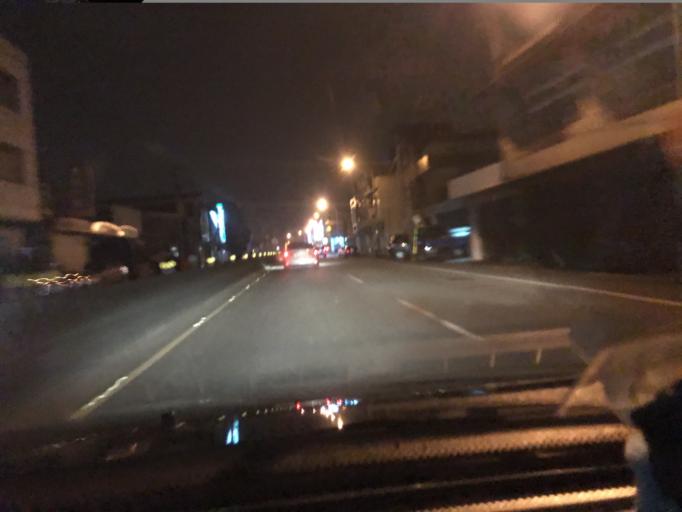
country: TW
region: Taiwan
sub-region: Hsinchu
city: Zhubei
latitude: 24.8013
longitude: 121.0519
